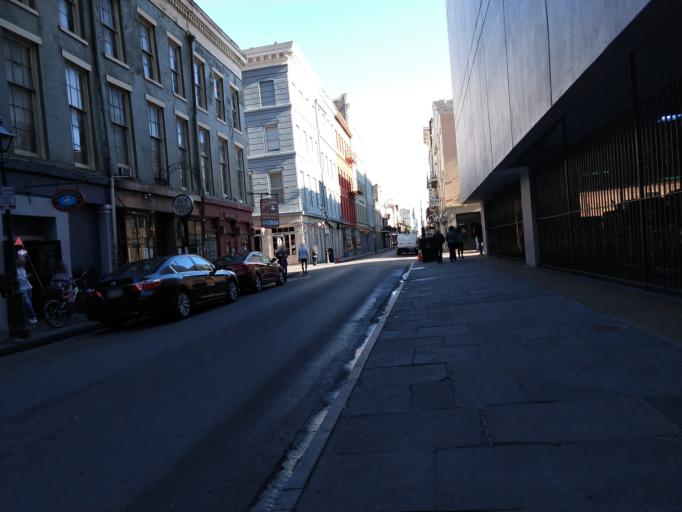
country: US
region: Louisiana
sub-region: Orleans Parish
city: New Orleans
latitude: 29.9533
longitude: -90.0676
